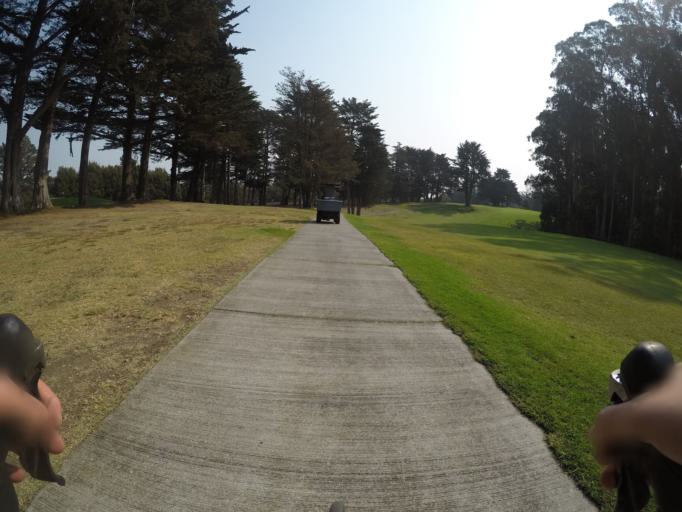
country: US
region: California
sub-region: Santa Cruz County
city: Live Oak
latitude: 36.9960
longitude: -121.9953
